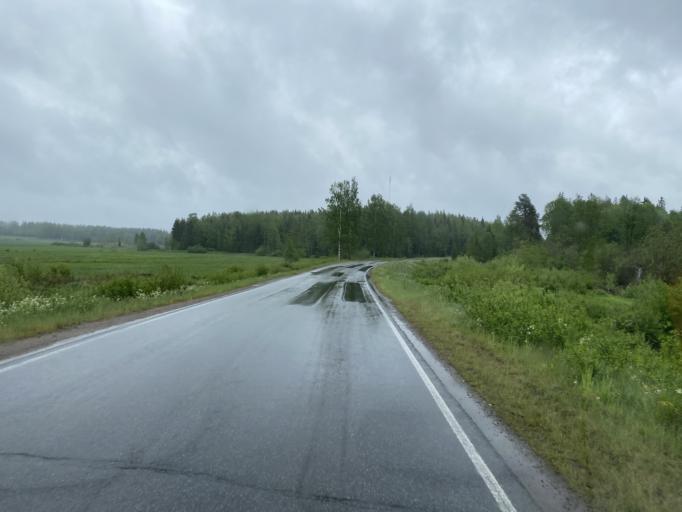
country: FI
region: Pirkanmaa
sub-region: Etelae-Pirkanmaa
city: Urjala
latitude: 61.0372
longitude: 23.4736
